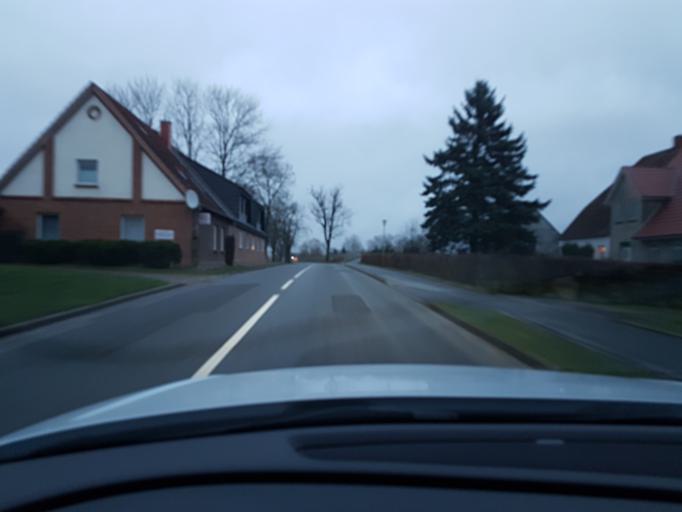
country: DE
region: Mecklenburg-Vorpommern
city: Satow-Oberhagen
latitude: 53.9892
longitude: 11.8985
